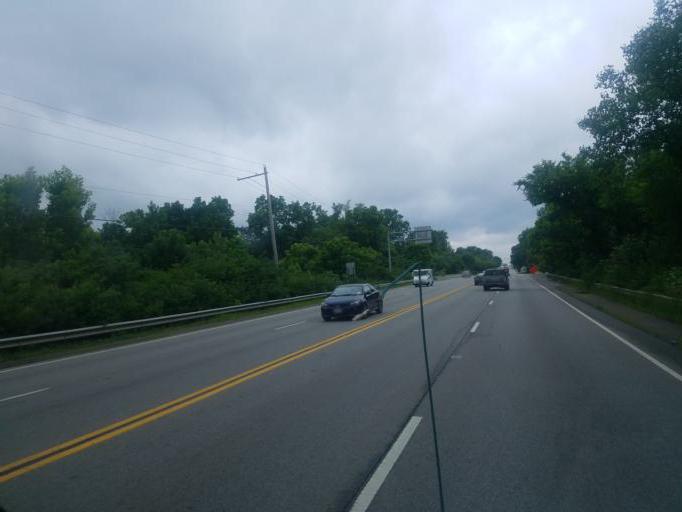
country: US
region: Ohio
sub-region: Franklin County
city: Whitehall
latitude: 39.9774
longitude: -82.8636
